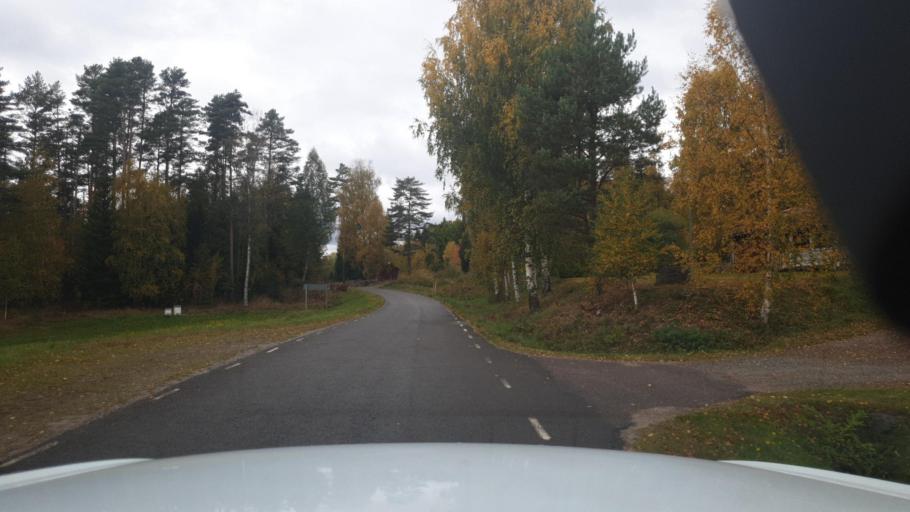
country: SE
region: Vaermland
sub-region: Eda Kommun
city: Charlottenberg
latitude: 60.0192
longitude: 12.6369
